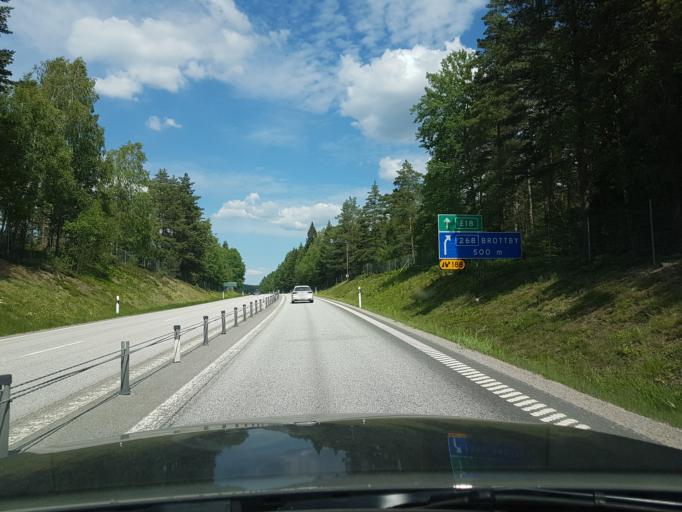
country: SE
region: Stockholm
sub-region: Osterakers Kommun
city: Akersberga
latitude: 59.5507
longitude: 18.2281
